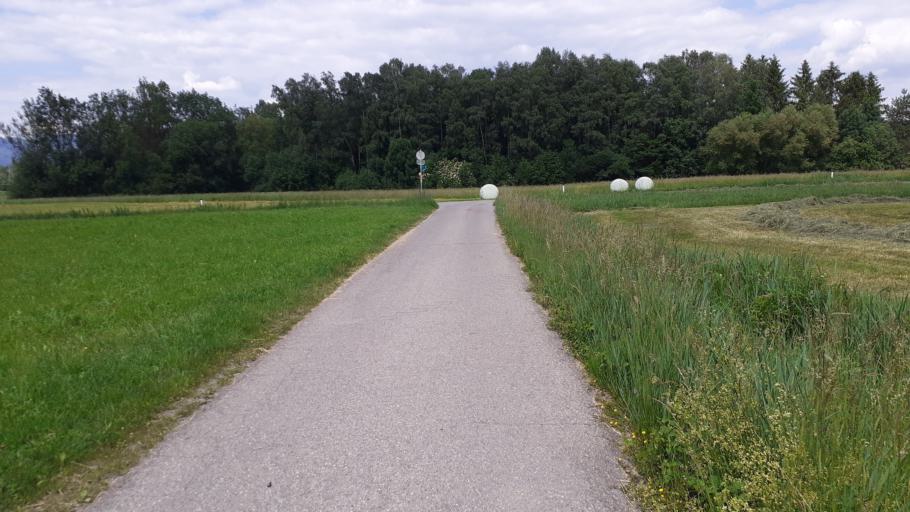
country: AT
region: Vorarlberg
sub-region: Politischer Bezirk Feldkirch
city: Koblach
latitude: 47.3143
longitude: 9.6124
